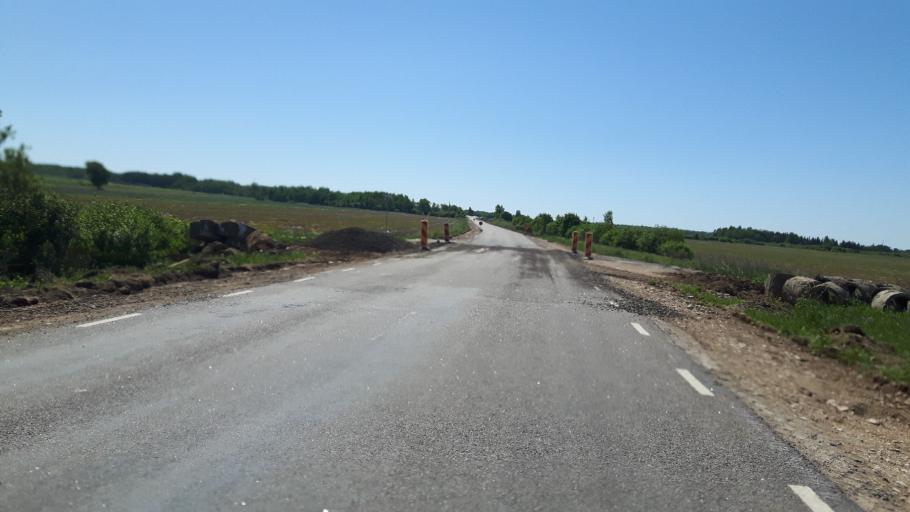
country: EE
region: Ida-Virumaa
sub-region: Narva-Joesuu linn
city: Narva-Joesuu
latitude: 59.3866
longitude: 27.9205
